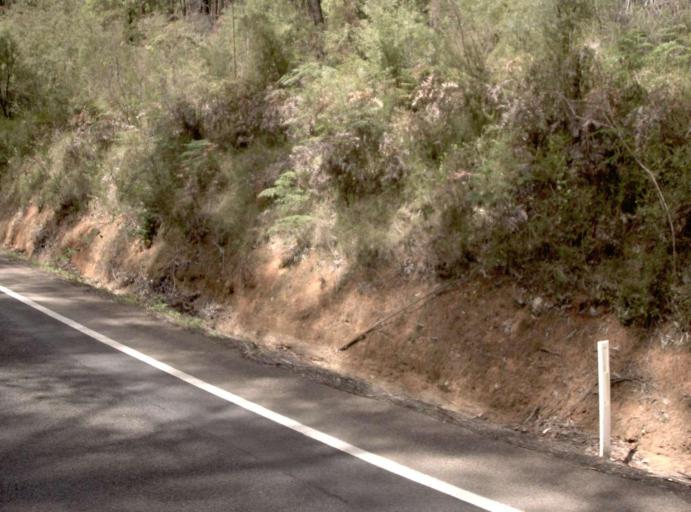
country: AU
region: New South Wales
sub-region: Bombala
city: Bombala
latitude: -37.5386
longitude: 149.3679
